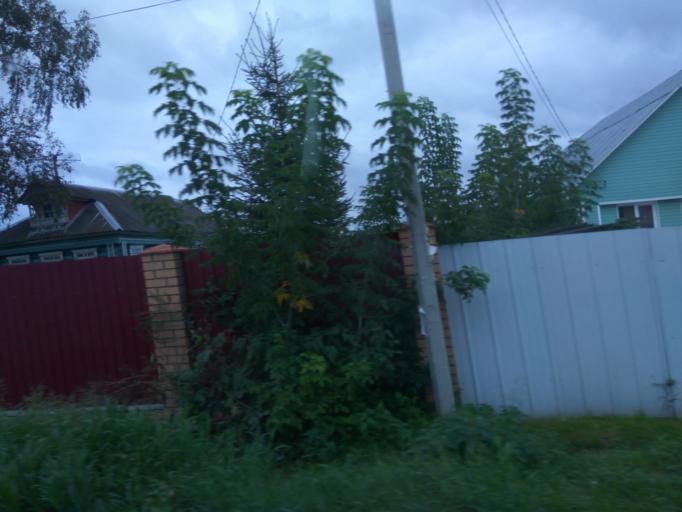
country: RU
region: Moskovskaya
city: Malyshevo
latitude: 55.4996
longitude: 38.3445
